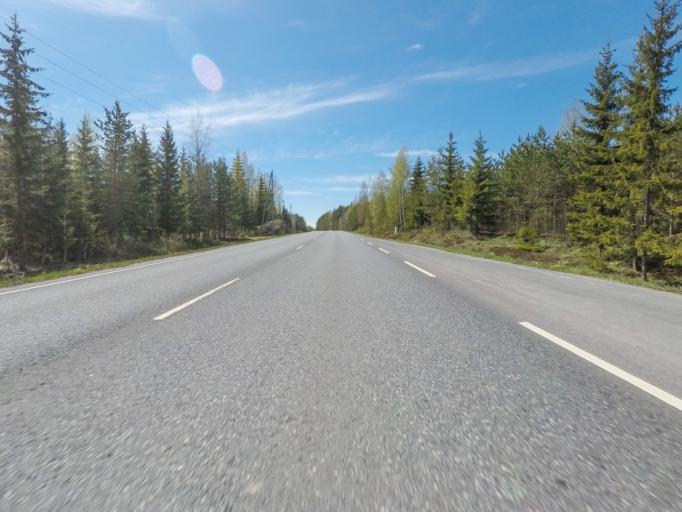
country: FI
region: Haeme
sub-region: Forssa
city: Humppila
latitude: 60.9853
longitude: 23.4474
